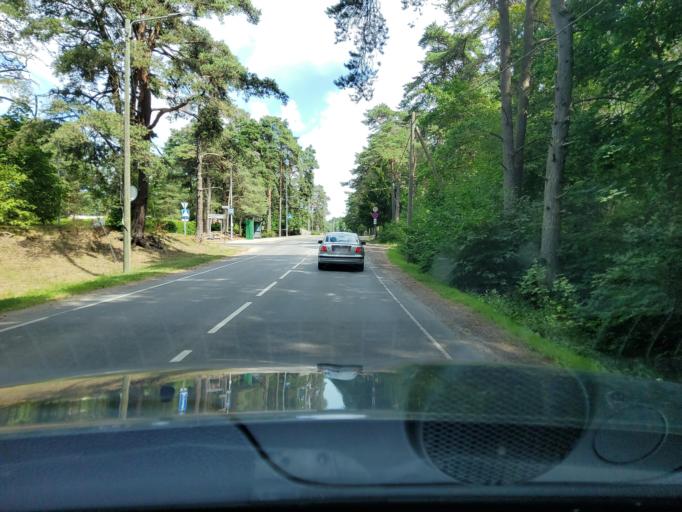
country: EE
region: Harju
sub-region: Tallinna linn
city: Kose
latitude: 59.4711
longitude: 24.8760
